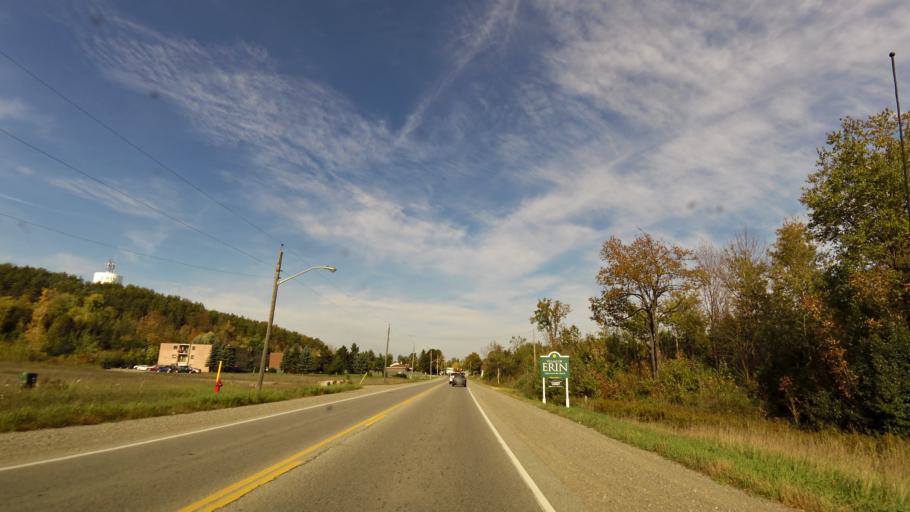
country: CA
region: Ontario
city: Orangeville
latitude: 43.7623
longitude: -80.0602
